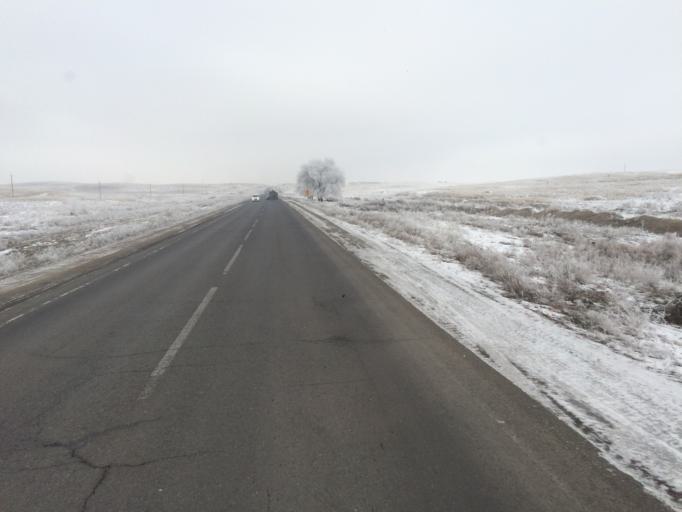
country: KG
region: Chuy
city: Bystrovka
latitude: 43.3206
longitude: 75.9989
